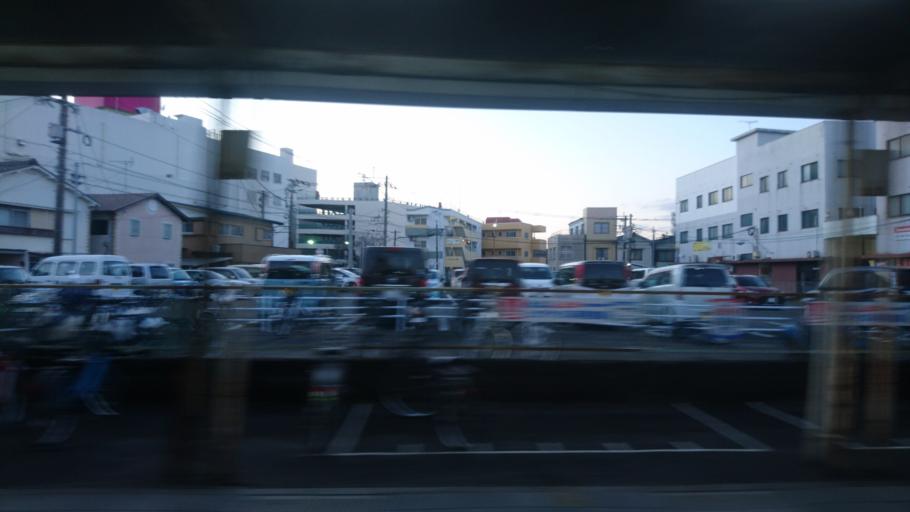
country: JP
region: Miyazaki
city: Miyazaki-shi
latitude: 31.8947
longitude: 131.4210
